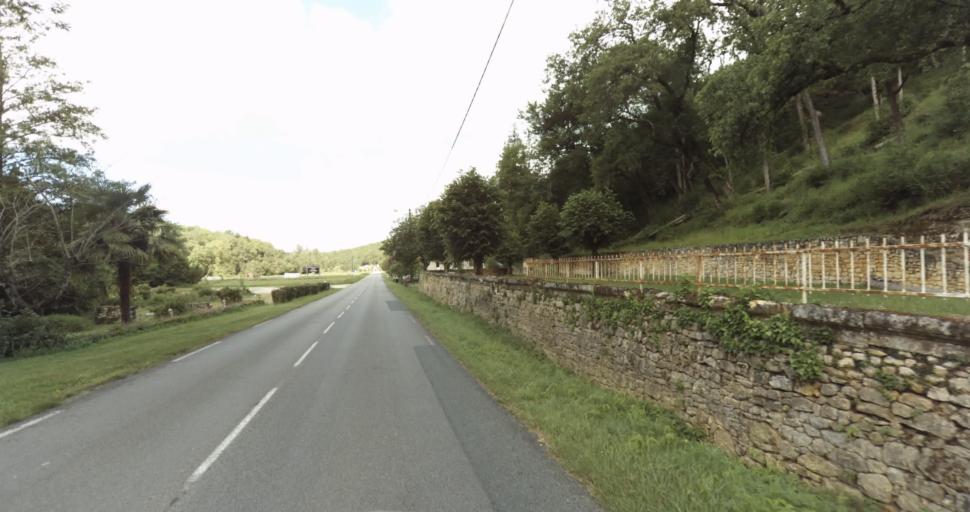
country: FR
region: Aquitaine
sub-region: Departement de la Dordogne
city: Lalinde
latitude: 44.8021
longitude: 0.7358
